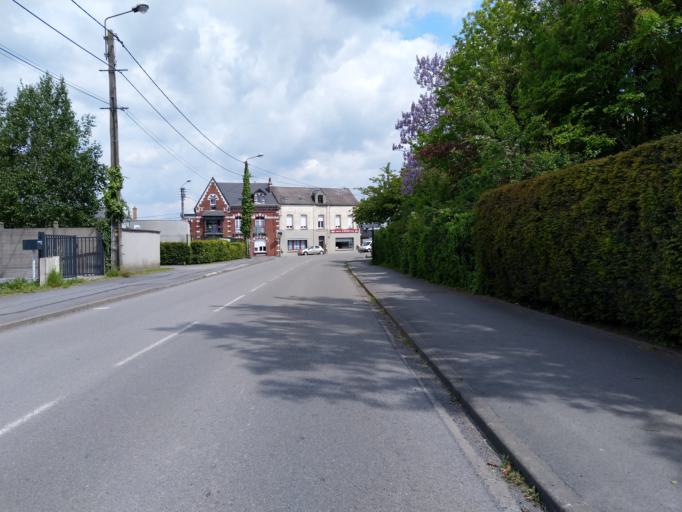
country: FR
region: Nord-Pas-de-Calais
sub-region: Departement du Nord
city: Le Quesnoy
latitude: 50.2531
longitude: 3.6427
